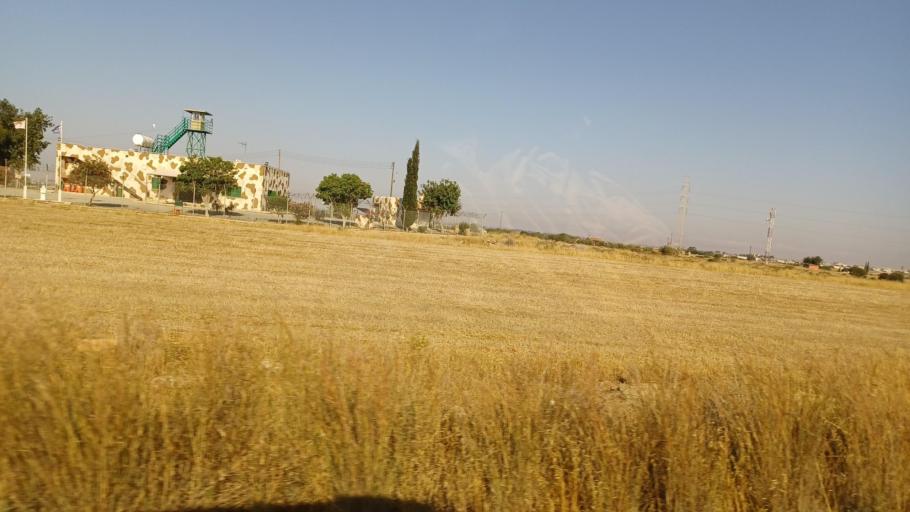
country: CY
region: Ammochostos
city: Frenaros
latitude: 35.0634
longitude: 33.9029
